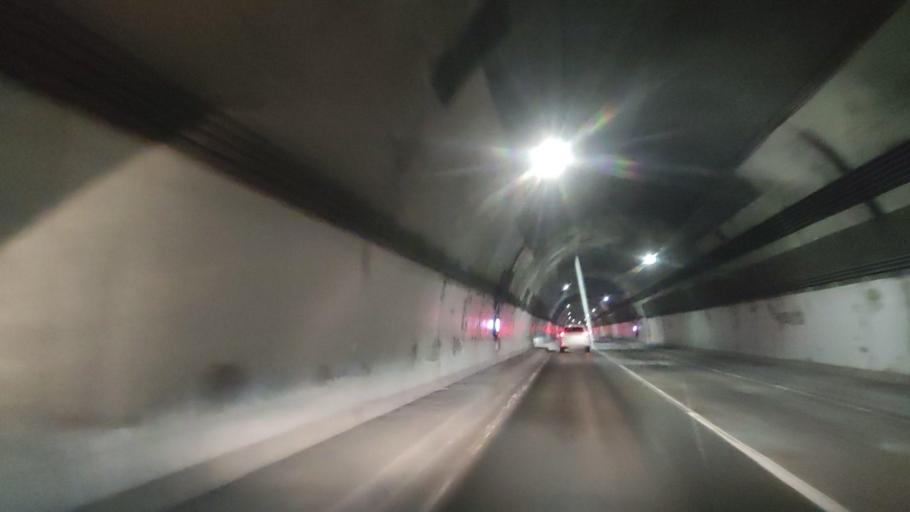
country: JP
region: Hokkaido
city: Ishikari
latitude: 43.4456
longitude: 141.4122
